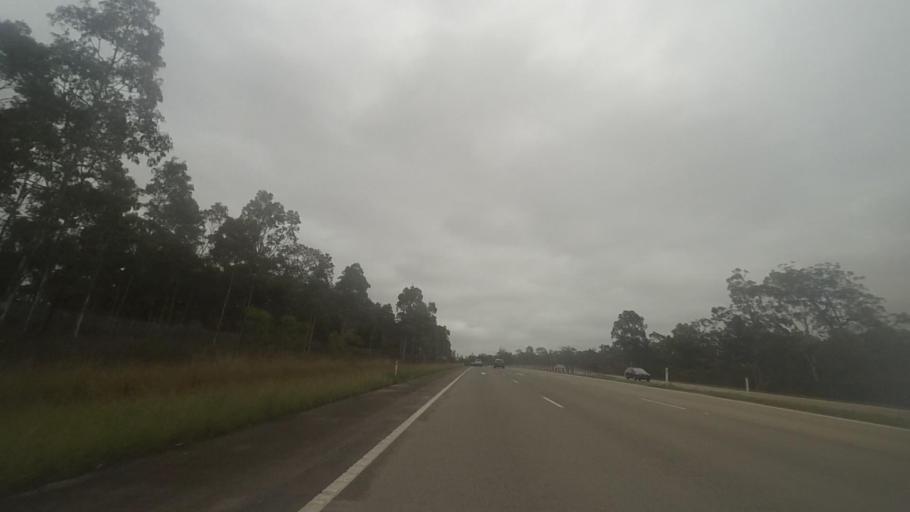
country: AU
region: New South Wales
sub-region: Port Stephens Shire
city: Medowie
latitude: -32.6826
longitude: 151.8144
